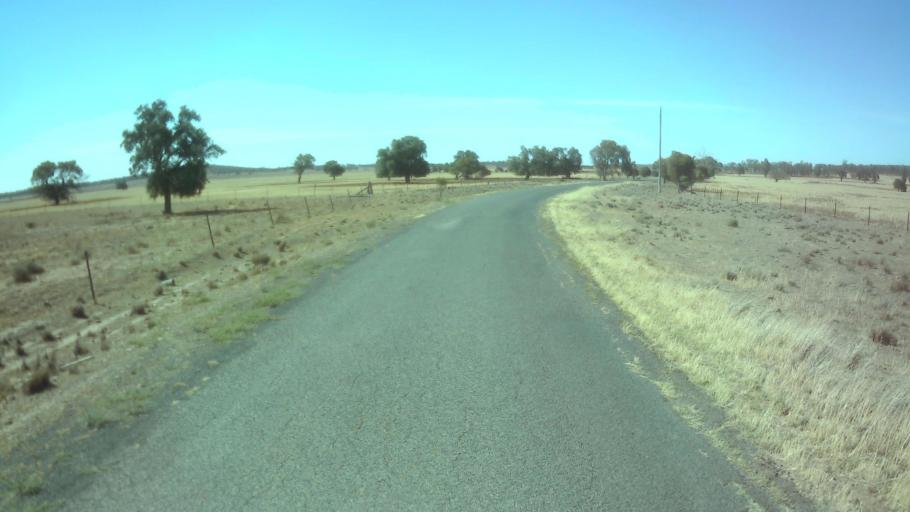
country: AU
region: New South Wales
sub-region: Forbes
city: Forbes
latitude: -33.7426
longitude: 147.7405
